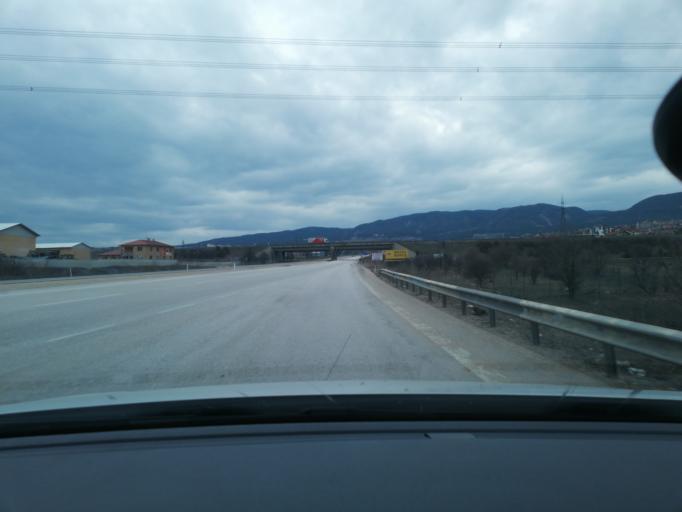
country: TR
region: Bolu
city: Gerede
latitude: 40.7790
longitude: 32.2163
